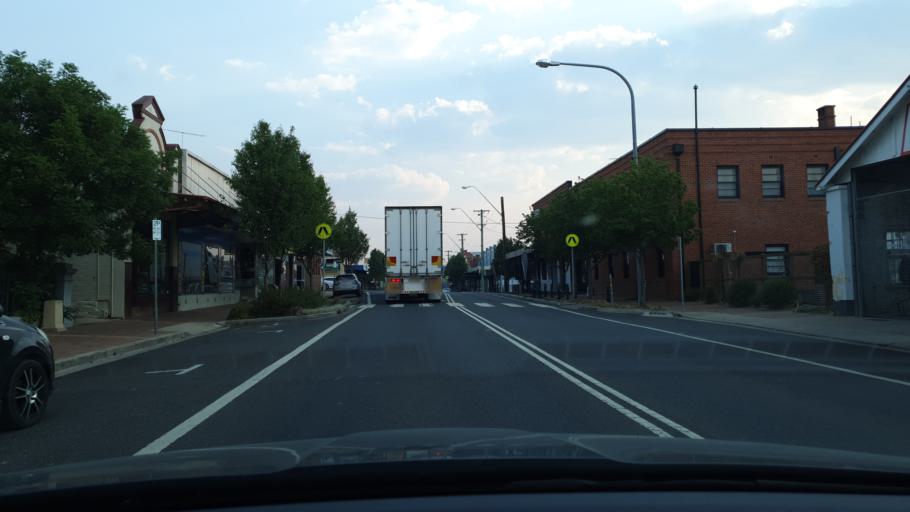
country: AU
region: New South Wales
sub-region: Tenterfield Municipality
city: Carrolls Creek
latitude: -29.0528
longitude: 152.0193
